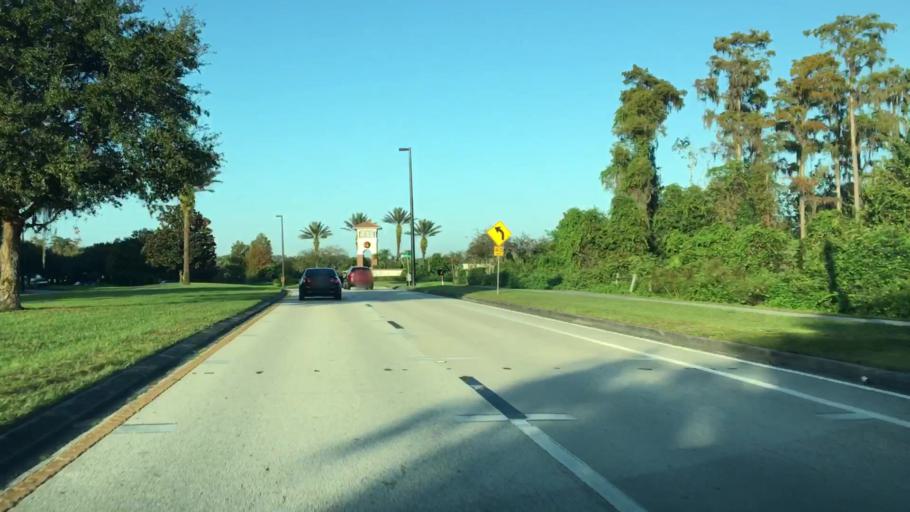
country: US
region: Florida
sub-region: Orange County
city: Azalea Park
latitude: 28.4786
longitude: -81.2542
